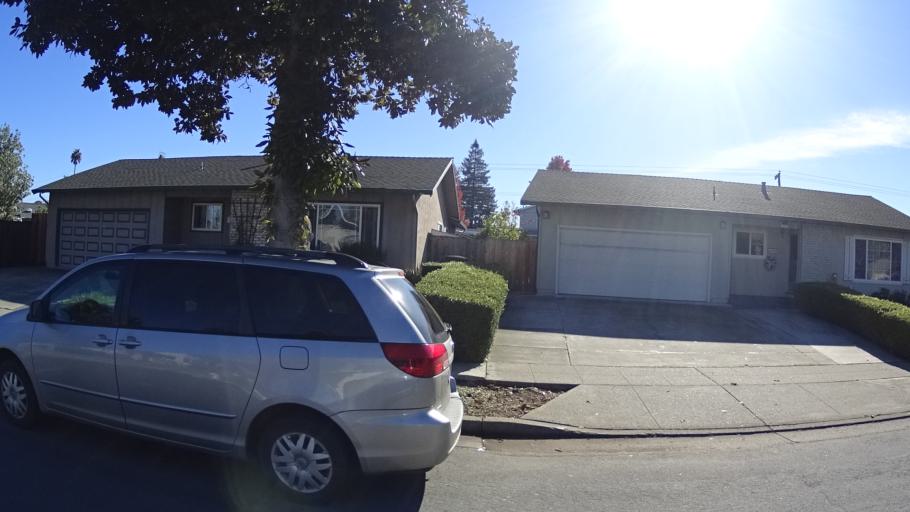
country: US
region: California
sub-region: Santa Clara County
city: Sunnyvale
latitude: 37.3625
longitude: -122.0114
